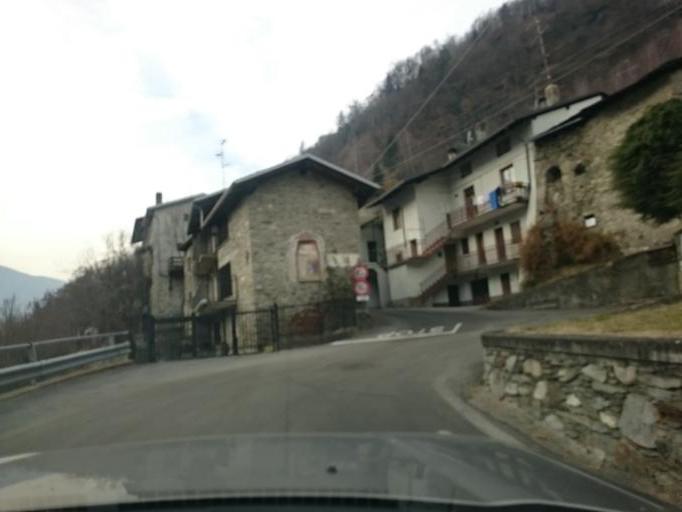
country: IT
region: Lombardy
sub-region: Provincia di Sondrio
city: Vervio
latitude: 46.2518
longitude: 10.2395
